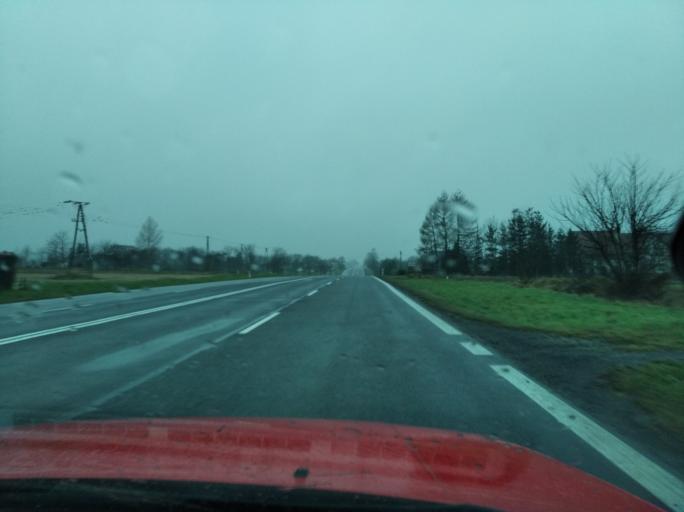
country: PL
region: Subcarpathian Voivodeship
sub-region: Powiat przeworski
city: Nowosielce
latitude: 50.0666
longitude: 22.3953
